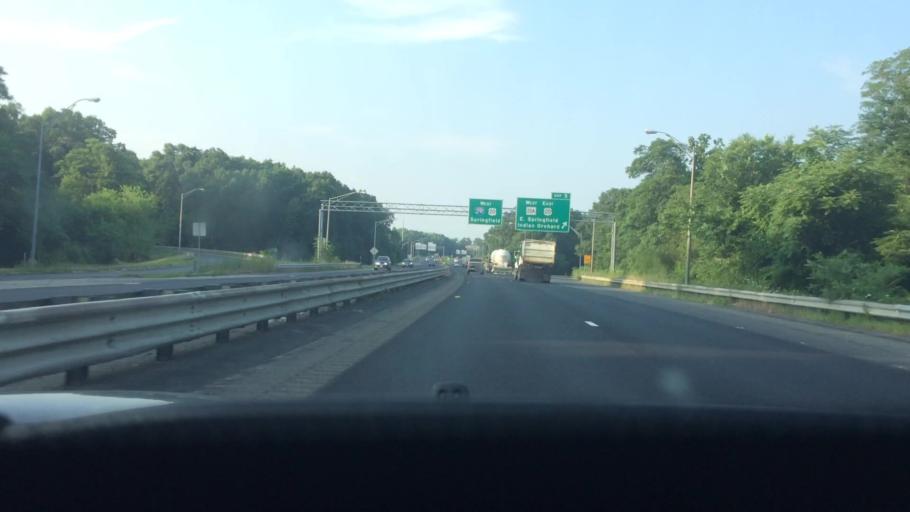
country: US
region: Massachusetts
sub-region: Hampden County
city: Chicopee
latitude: 42.1507
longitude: -72.5496
